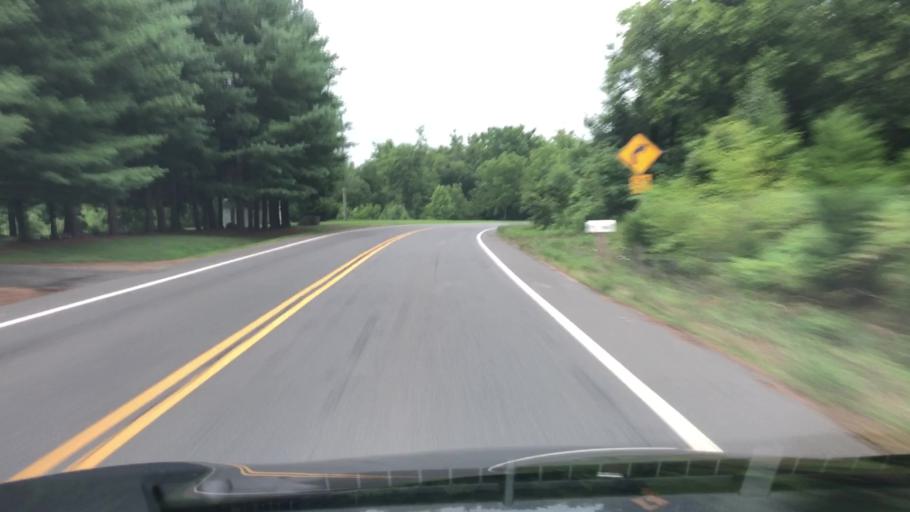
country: US
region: Virginia
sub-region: Prince William County
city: Nokesville
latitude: 38.6145
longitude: -77.6041
